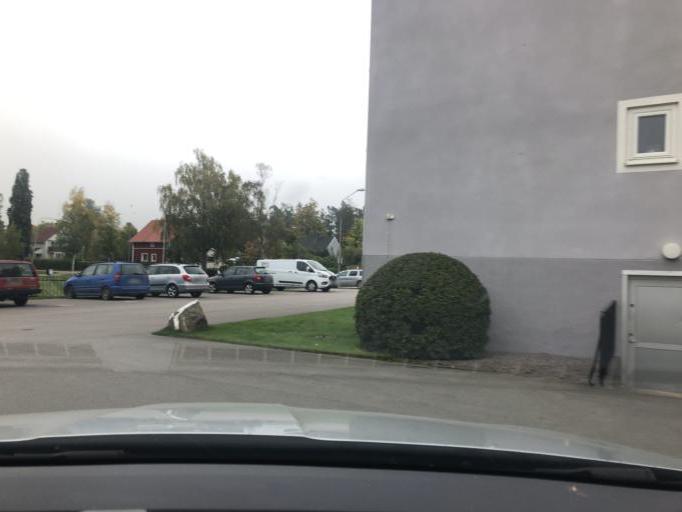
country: SE
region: Uppsala
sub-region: Osthammars Kommun
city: Gimo
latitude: 60.1741
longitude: 18.1872
